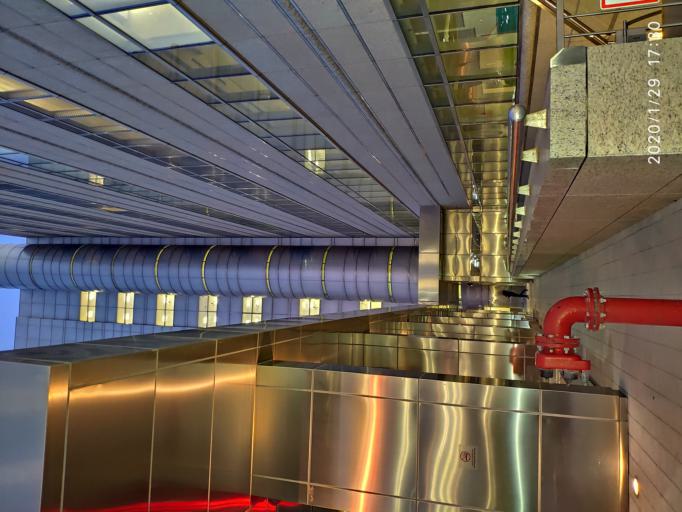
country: QA
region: Baladiyat ar Rayyan
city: Ar Rayyan
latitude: 25.3237
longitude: 51.4450
